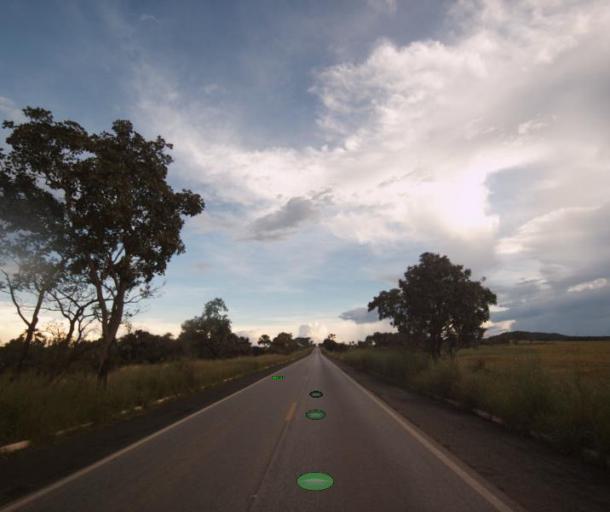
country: BR
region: Goias
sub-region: Uruacu
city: Uruacu
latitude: -14.0928
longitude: -49.1006
